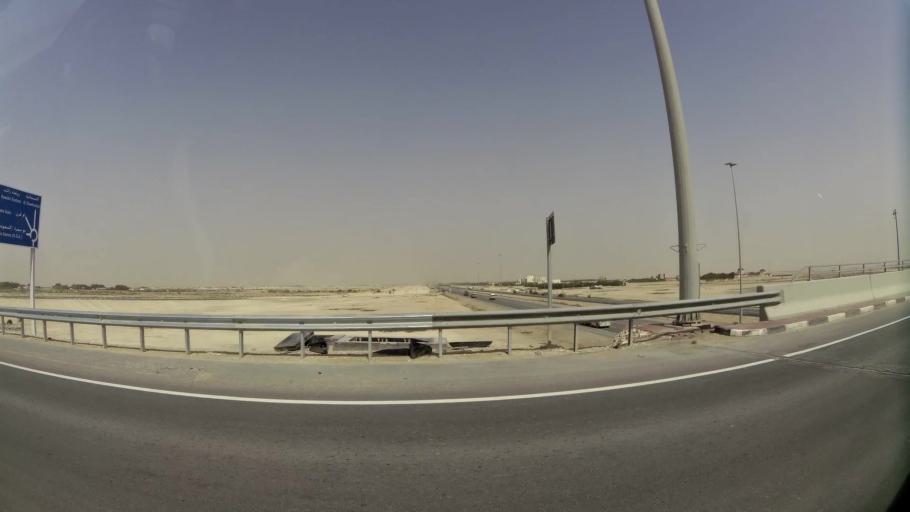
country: QA
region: Baladiyat ar Rayyan
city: Ar Rayyan
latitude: 25.1553
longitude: 51.2769
